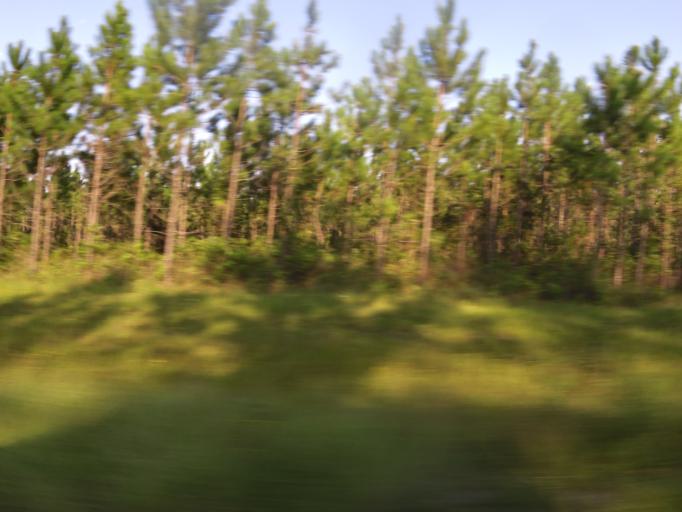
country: US
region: Florida
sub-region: Duval County
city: Baldwin
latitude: 30.3515
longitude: -82.0093
